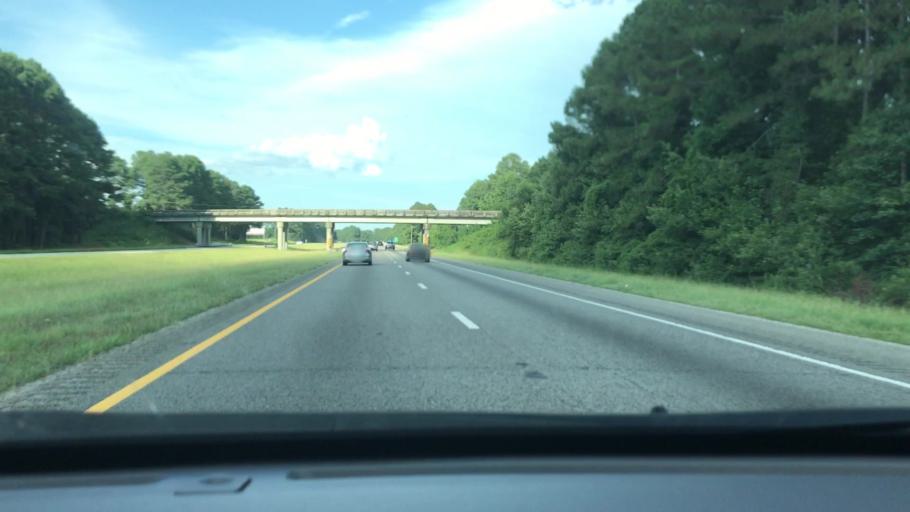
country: US
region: South Carolina
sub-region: Dillon County
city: Dillon
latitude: 34.4066
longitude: -79.4344
